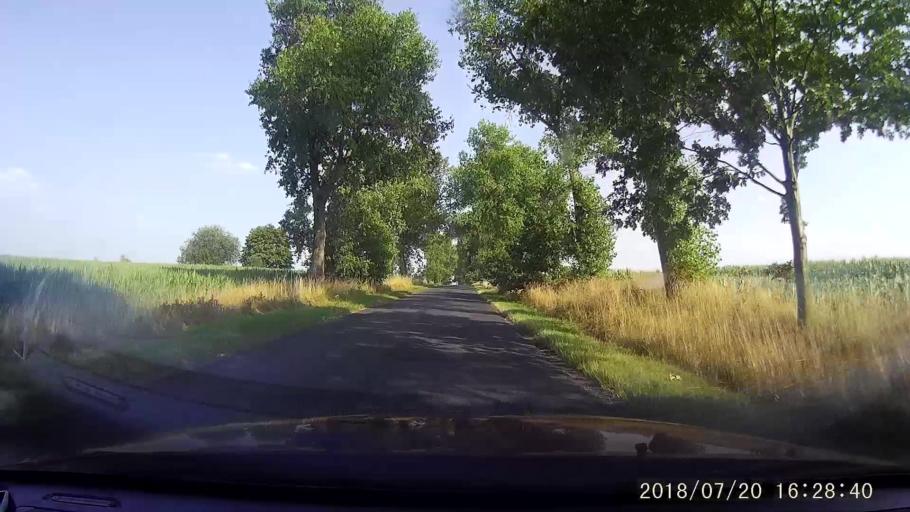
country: PL
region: Lower Silesian Voivodeship
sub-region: Powiat zgorzelecki
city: Sulikow
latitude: 51.1178
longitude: 15.0593
